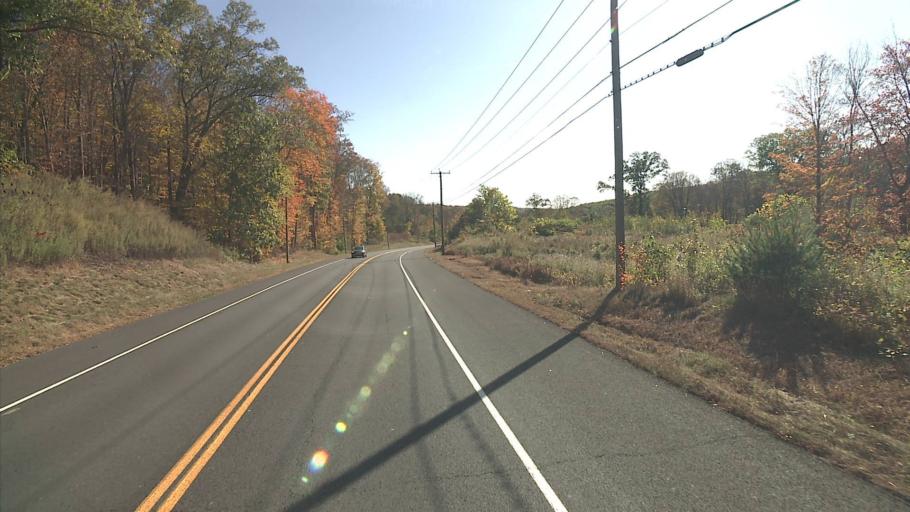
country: US
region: Connecticut
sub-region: Tolland County
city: Rockville
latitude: 41.7827
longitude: -72.4258
